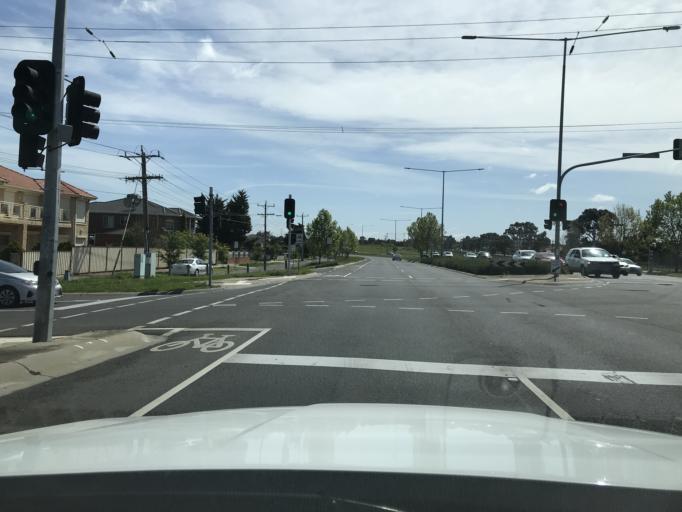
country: AU
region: Victoria
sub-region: Hume
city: Broadmeadows
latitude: -37.6712
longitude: 144.9235
